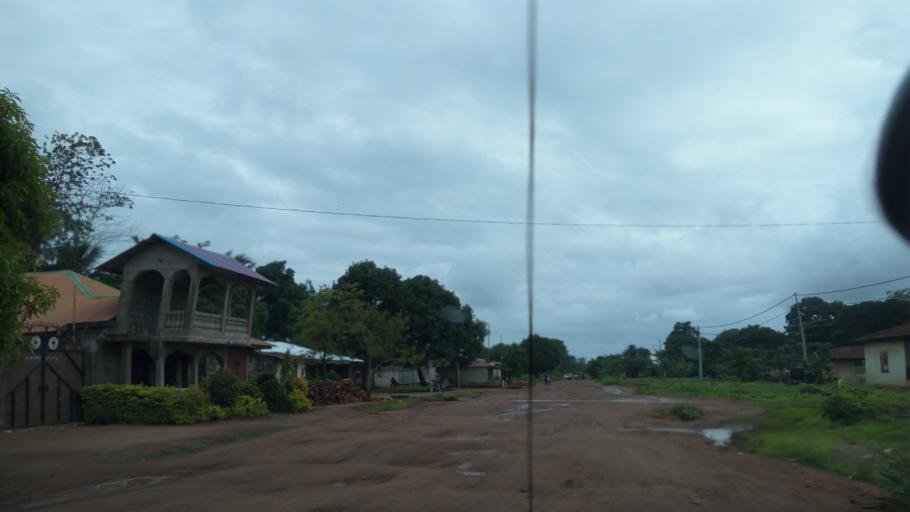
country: SL
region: Northern Province
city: Tintafor
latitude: 8.6245
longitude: -13.2149
